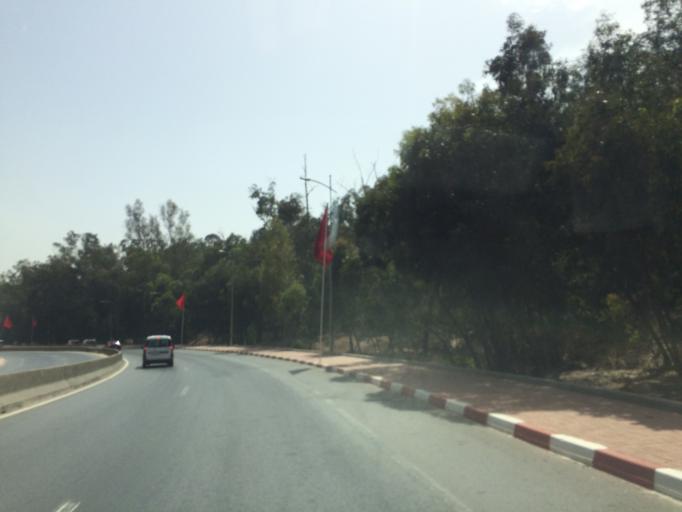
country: MA
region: Rabat-Sale-Zemmour-Zaer
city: Sale
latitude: 34.0277
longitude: -6.7963
